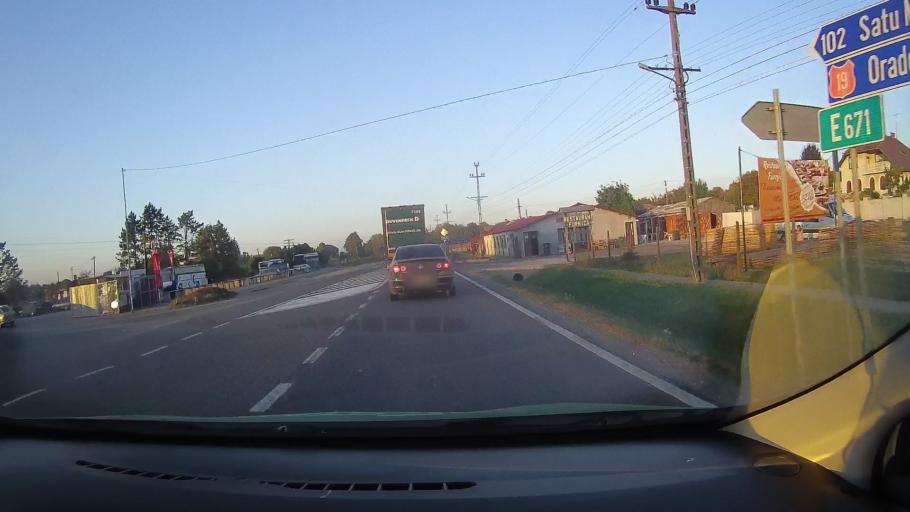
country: RO
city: Dioszeg
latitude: 47.2934
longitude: 22.0110
